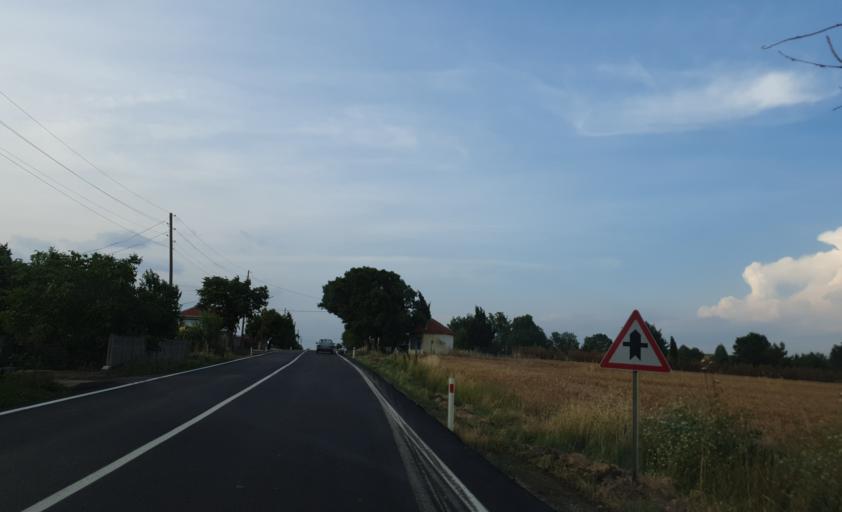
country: TR
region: Tekirdag
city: Hayrabolu
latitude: 41.2916
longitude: 27.1341
